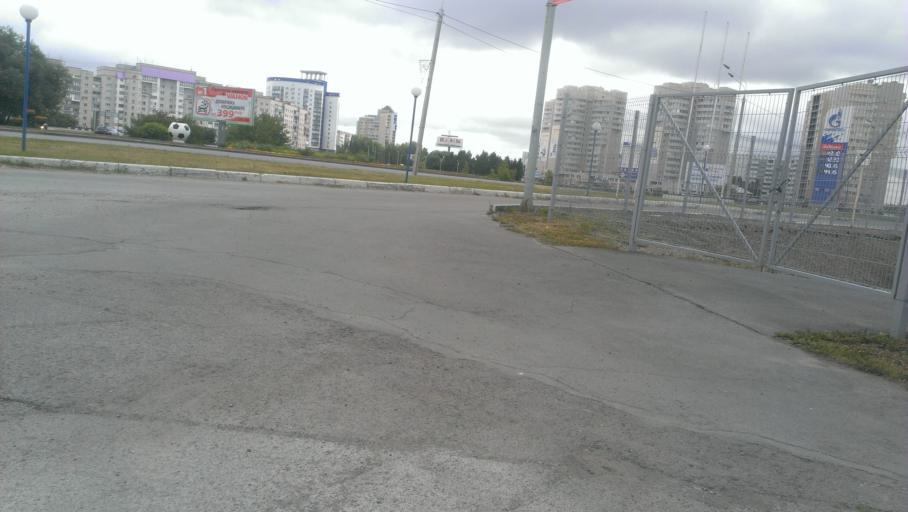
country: RU
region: Altai Krai
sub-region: Gorod Barnaulskiy
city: Barnaul
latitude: 53.3419
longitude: 83.6922
